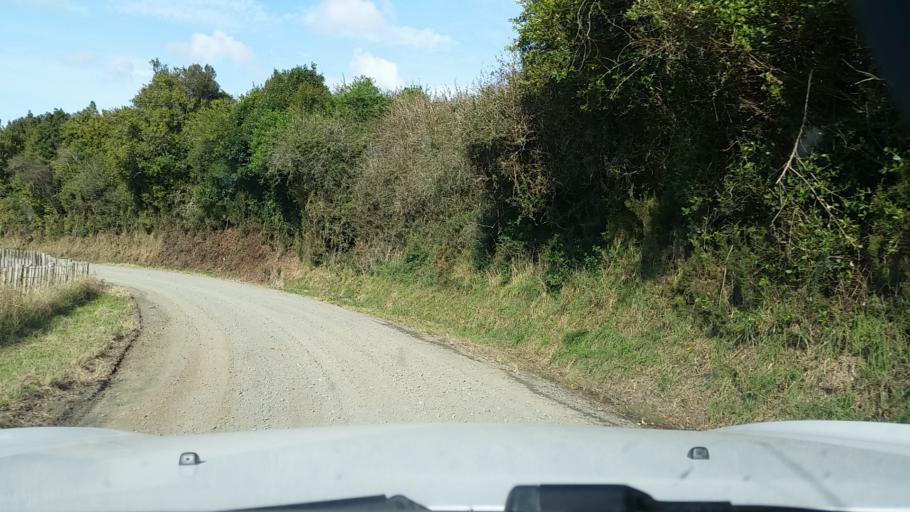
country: NZ
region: Waikato
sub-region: Matamata-Piako District
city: Matamata
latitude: -37.8037
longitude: 175.6327
